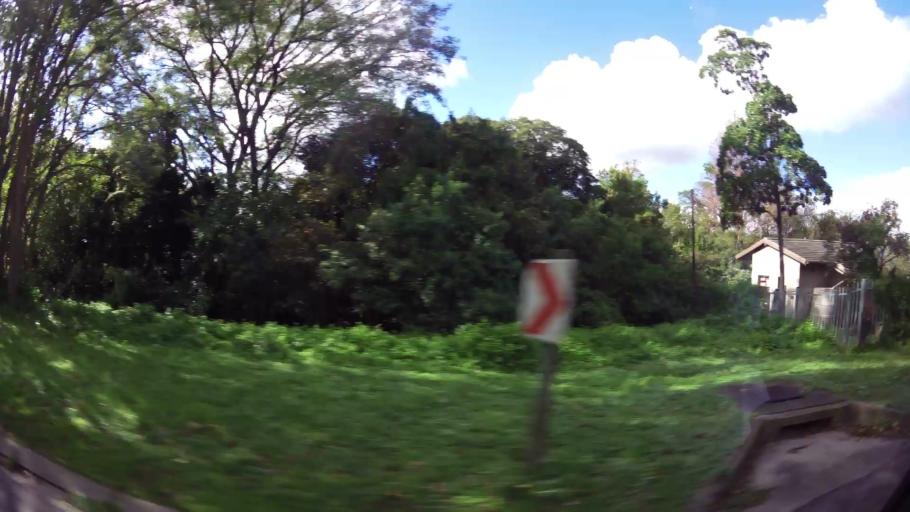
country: ZA
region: Western Cape
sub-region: Eden District Municipality
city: Knysna
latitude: -34.0423
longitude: 23.0728
